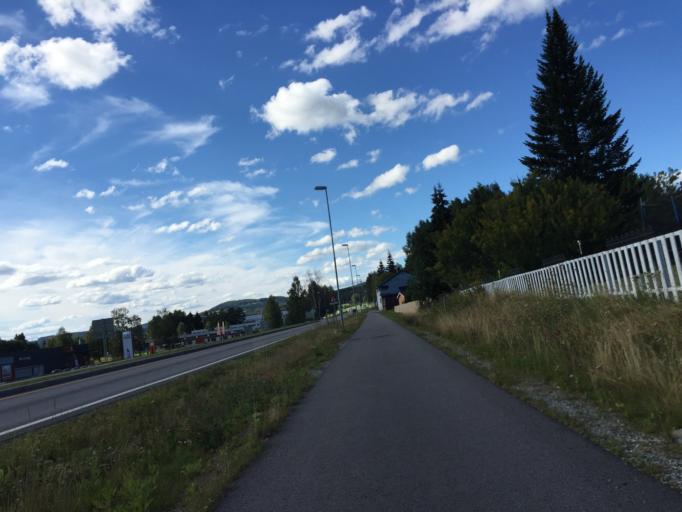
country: NO
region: Hedmark
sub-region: Kongsvinger
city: Kongsvinger
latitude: 60.2036
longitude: 11.9763
